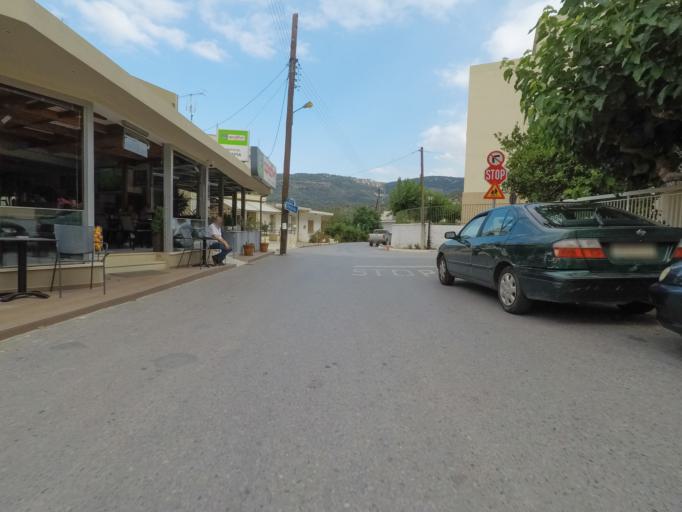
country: GR
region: Crete
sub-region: Nomos Lasithiou
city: Kritsa
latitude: 35.1565
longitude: 25.6467
